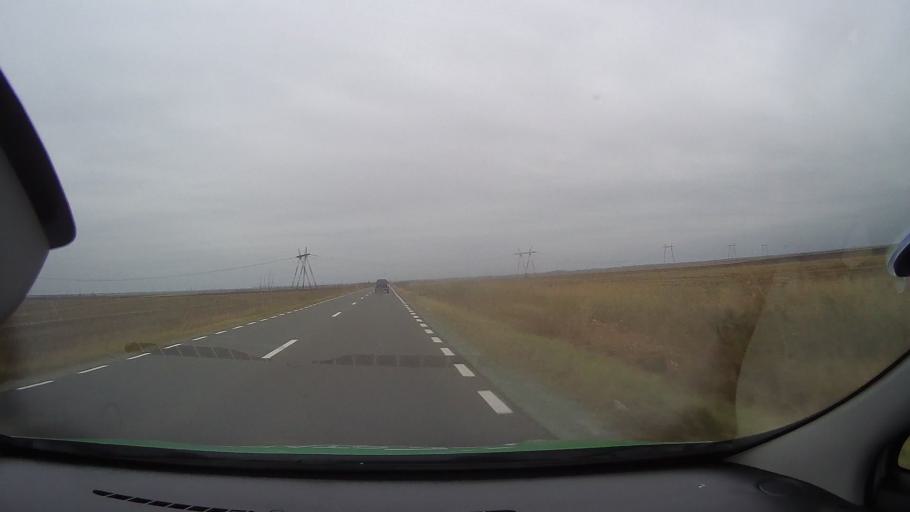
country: RO
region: Ialomita
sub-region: Comuna Gheorghe Lazar
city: Gheorghe Lazar
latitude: 44.6526
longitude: 27.4086
